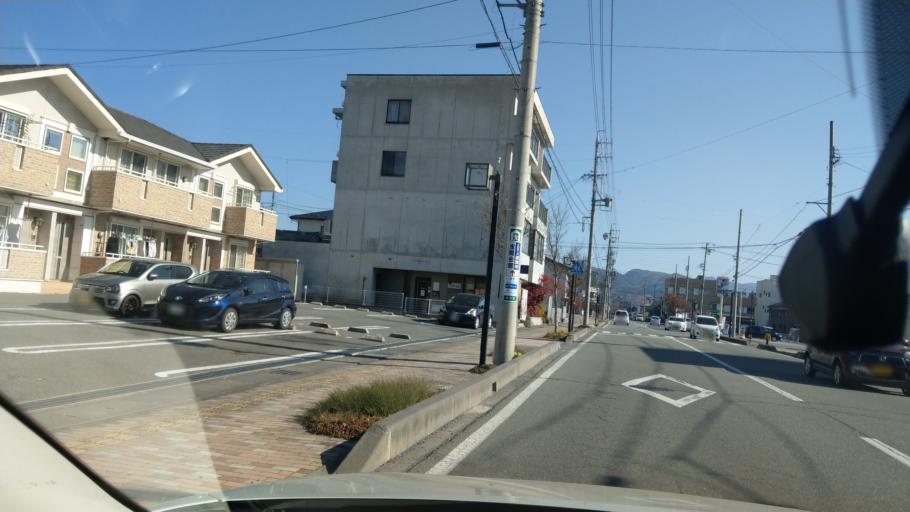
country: JP
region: Nagano
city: Saku
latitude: 36.2743
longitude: 138.4764
